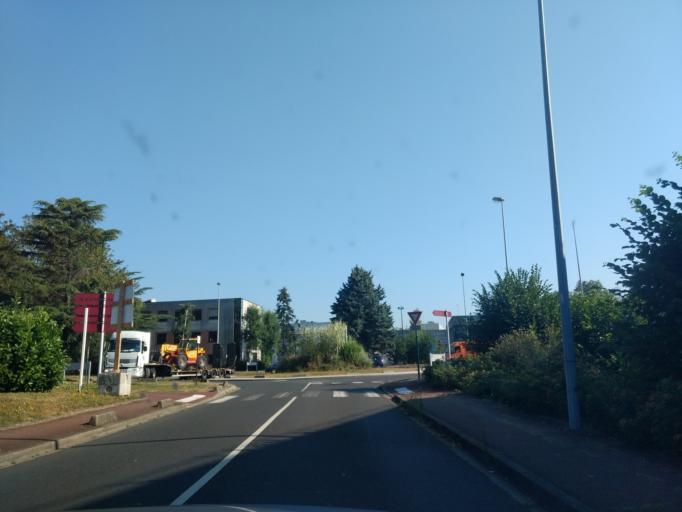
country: FR
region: Ile-de-France
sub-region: Departement des Yvelines
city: Jouy-en-Josas
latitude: 48.7800
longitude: 2.1691
